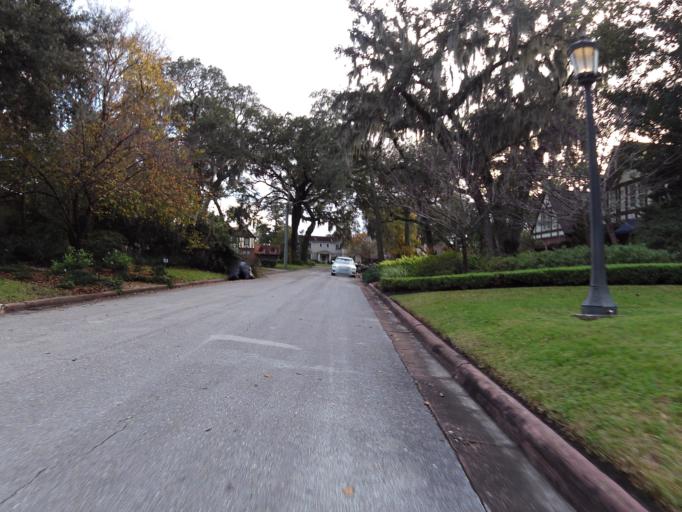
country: US
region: Florida
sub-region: Duval County
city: Jacksonville
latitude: 30.2823
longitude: -81.6587
